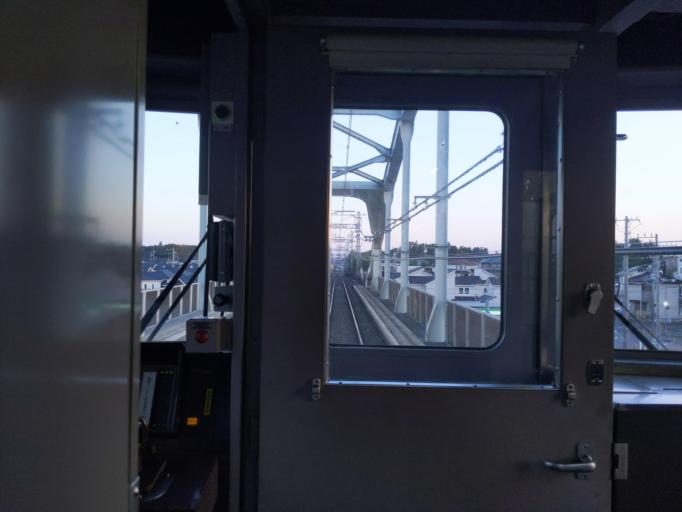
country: JP
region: Chiba
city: Noda
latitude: 35.9632
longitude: 139.8575
